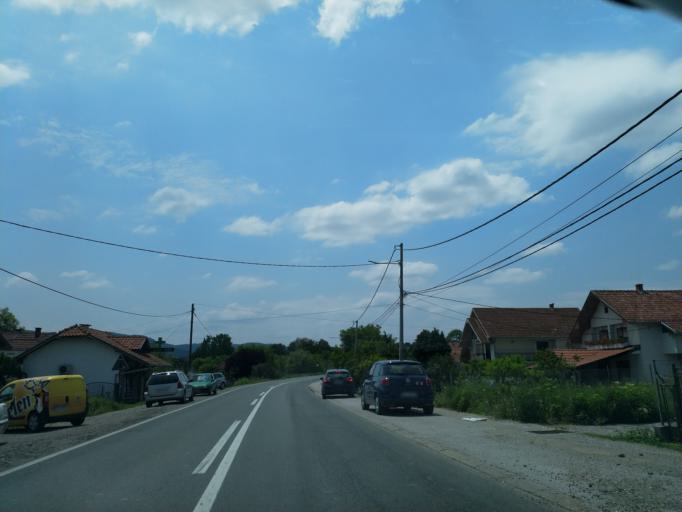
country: RS
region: Central Serbia
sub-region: Toplicki Okrug
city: Blace
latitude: 43.4499
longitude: 21.2354
